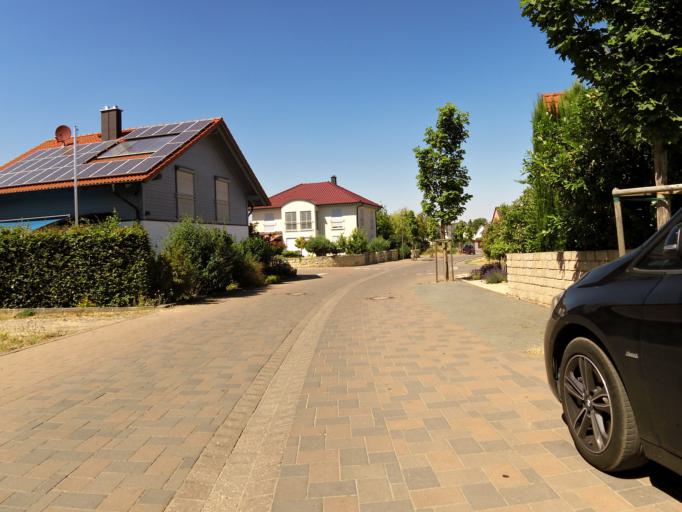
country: DE
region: Rheinland-Pfalz
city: Ruppertsberg
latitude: 49.3975
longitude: 8.2006
